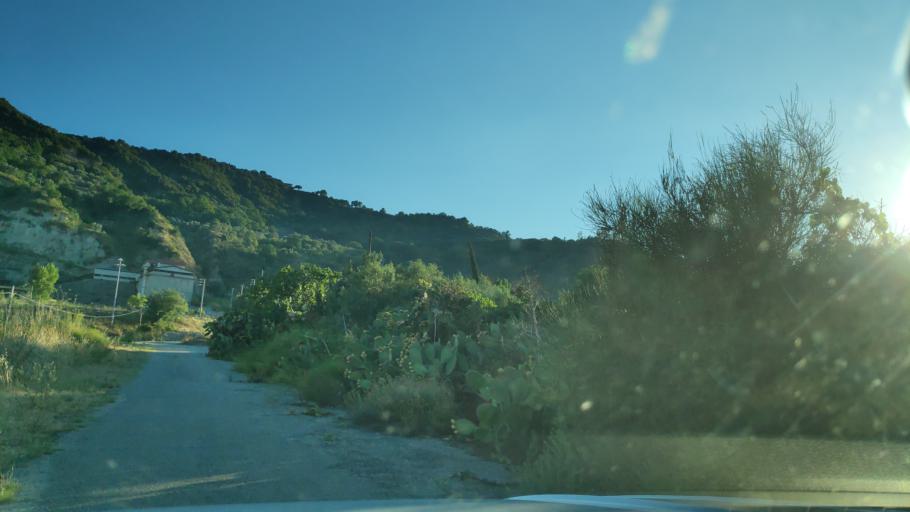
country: IT
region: Calabria
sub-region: Provincia di Reggio Calabria
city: Stilo
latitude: 38.4669
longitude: 16.4907
